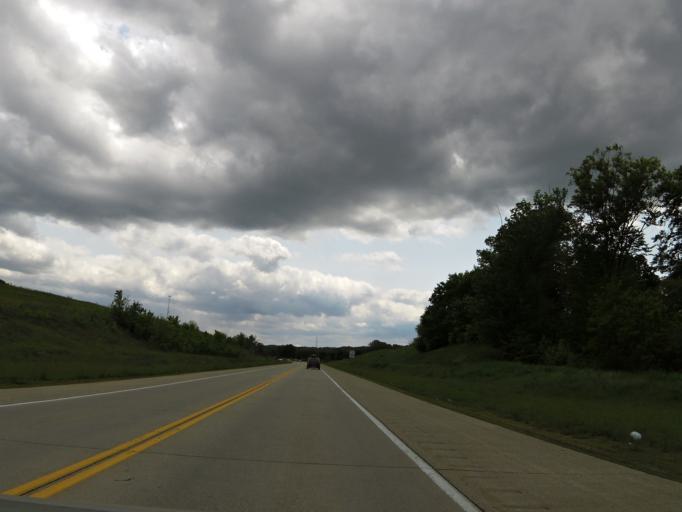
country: US
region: Ohio
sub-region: Meigs County
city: Pomeroy
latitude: 39.1587
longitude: -82.0353
